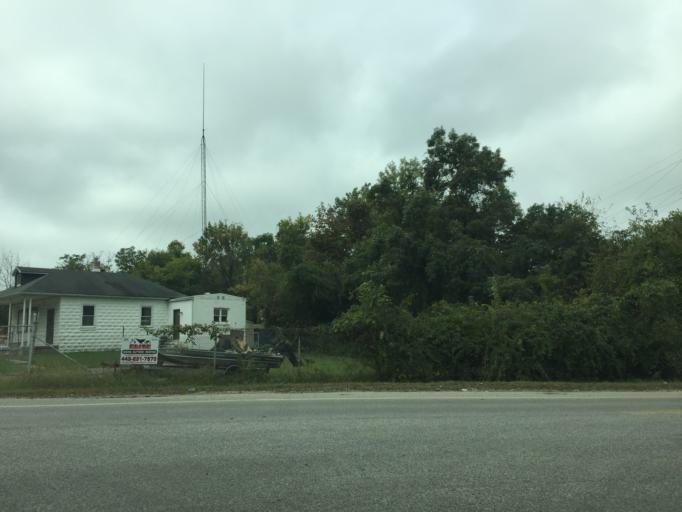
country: US
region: Maryland
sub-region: Baltimore County
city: Rossville
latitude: 39.3282
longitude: -76.4730
